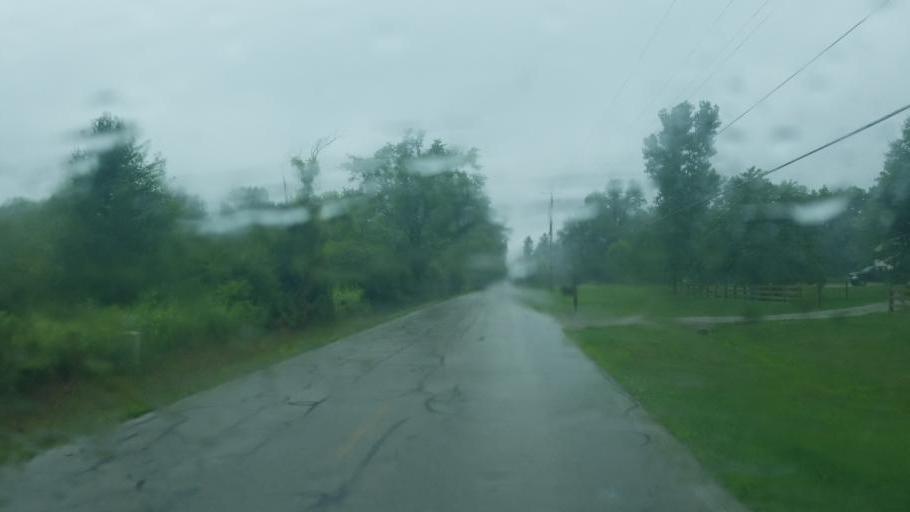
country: US
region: Ohio
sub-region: Delaware County
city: Sunbury
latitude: 40.2397
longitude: -82.9393
